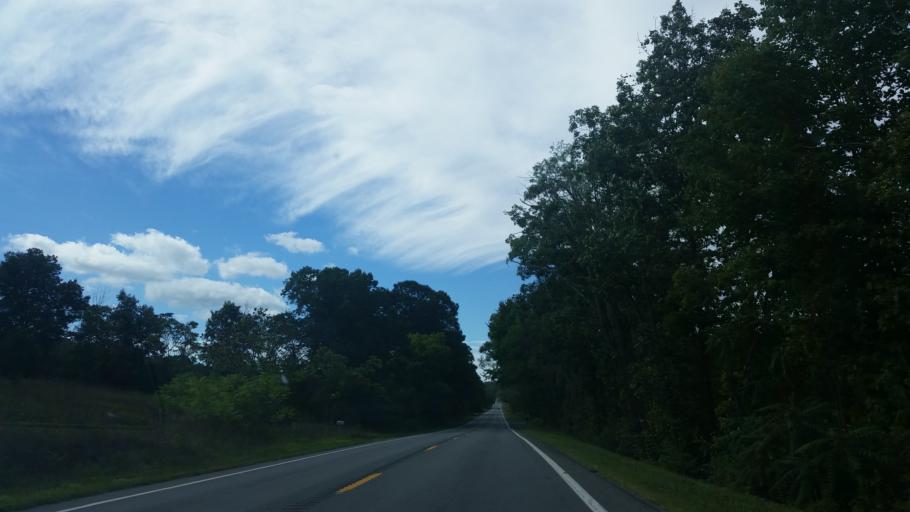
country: US
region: West Virginia
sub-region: Morgan County
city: Berkeley Springs
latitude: 39.5353
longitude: -78.2758
